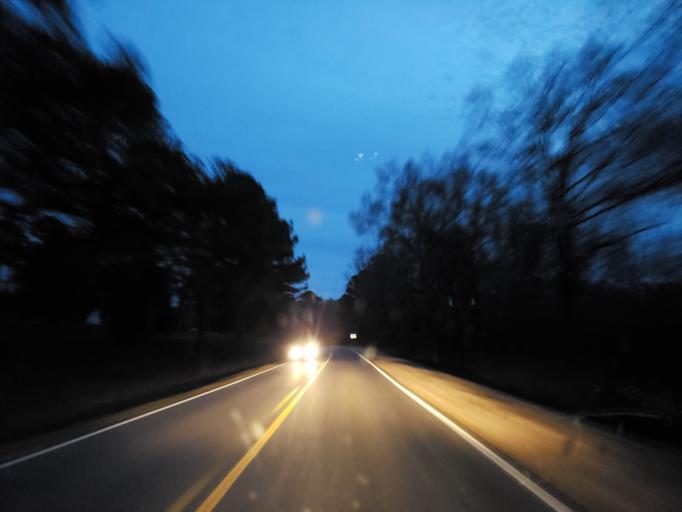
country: US
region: Alabama
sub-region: Greene County
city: Eutaw
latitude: 32.8723
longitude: -87.9281
